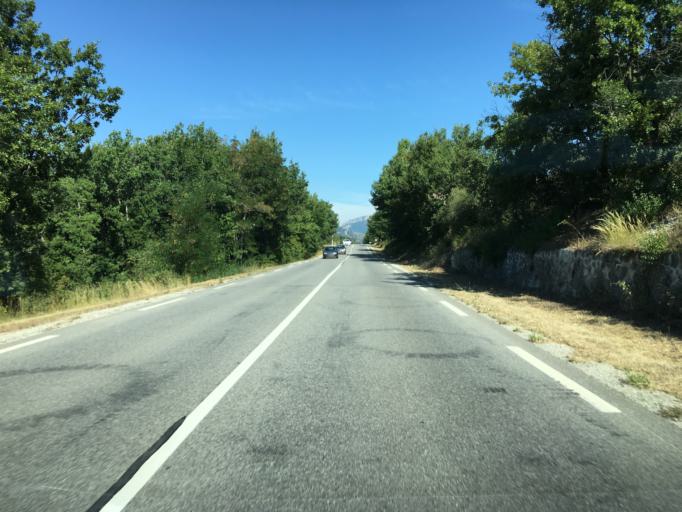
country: FR
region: Provence-Alpes-Cote d'Azur
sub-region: Departement des Hautes-Alpes
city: Serres
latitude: 44.3888
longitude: 5.7424
